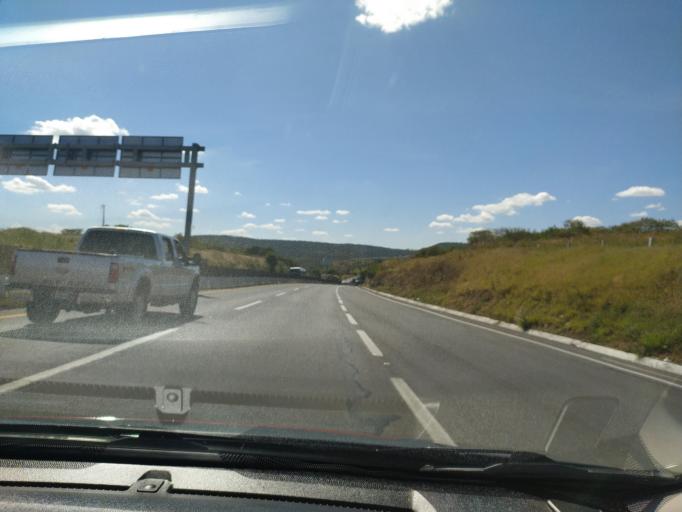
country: MX
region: Jalisco
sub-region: Tonala
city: Mismaloya (Fraccionamiento Pedregal de Santa Martha)
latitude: 20.6041
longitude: -103.1425
